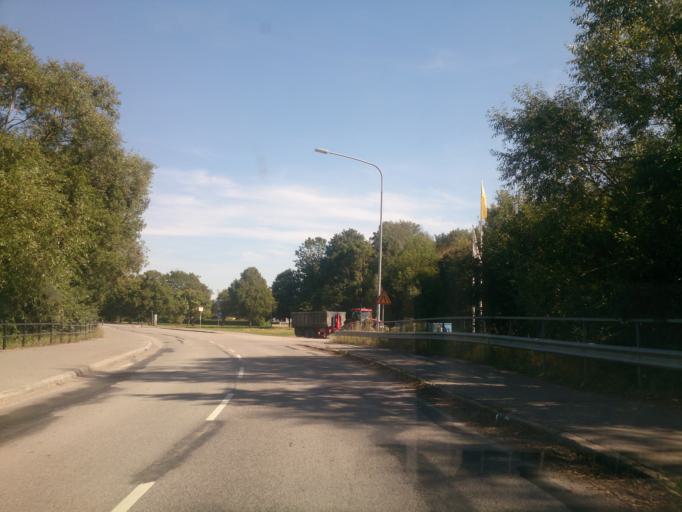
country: SE
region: OEstergoetland
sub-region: Norrkopings Kommun
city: Norrkoping
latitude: 58.5793
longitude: 16.2159
